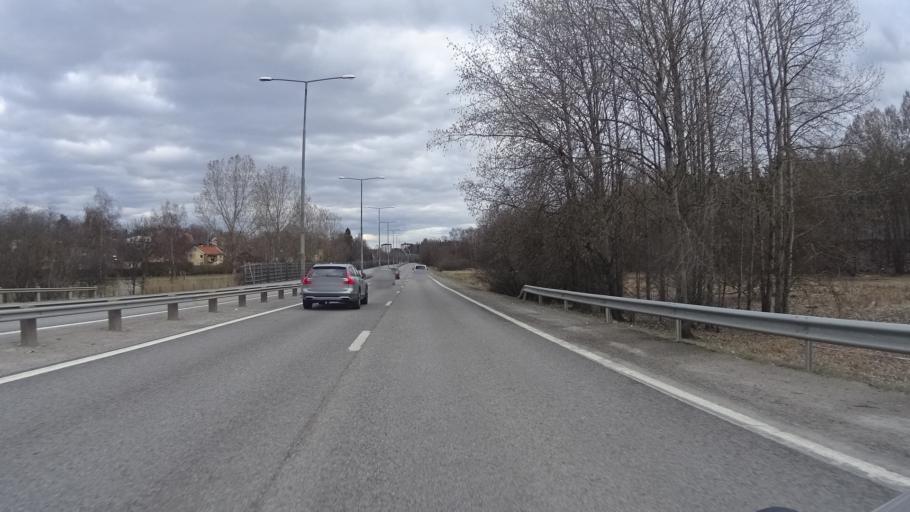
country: SE
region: Stockholm
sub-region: Stockholms Kommun
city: Arsta
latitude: 59.2706
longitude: 18.0168
